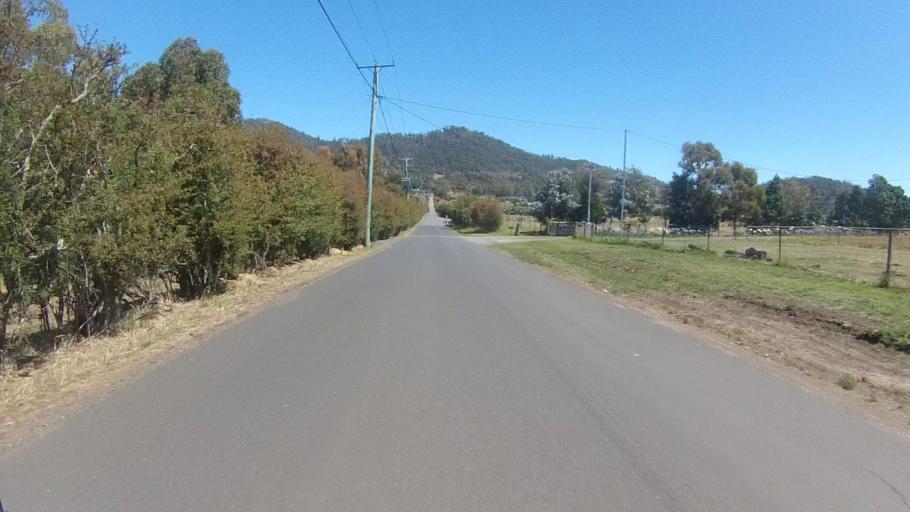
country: AU
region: Tasmania
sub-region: Clarence
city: Cambridge
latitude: -42.8417
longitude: 147.4614
